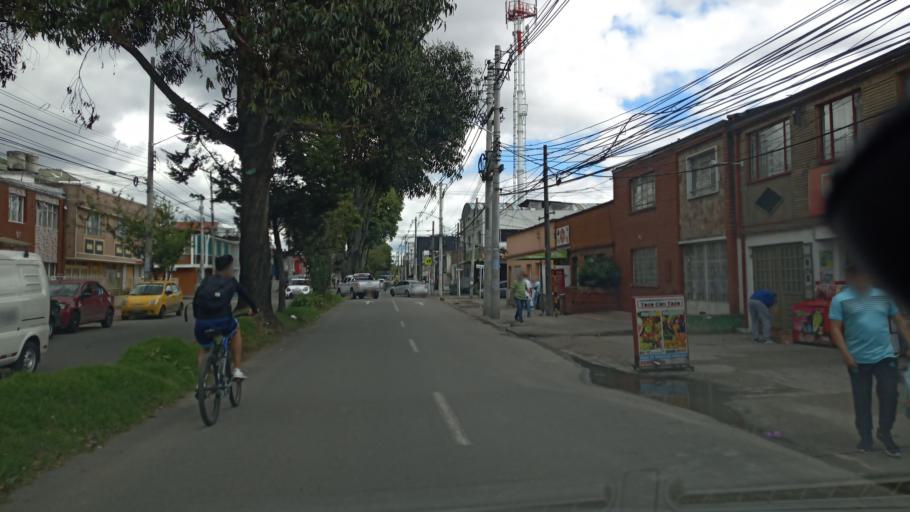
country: CO
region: Bogota D.C.
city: Bogota
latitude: 4.6692
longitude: -74.1406
